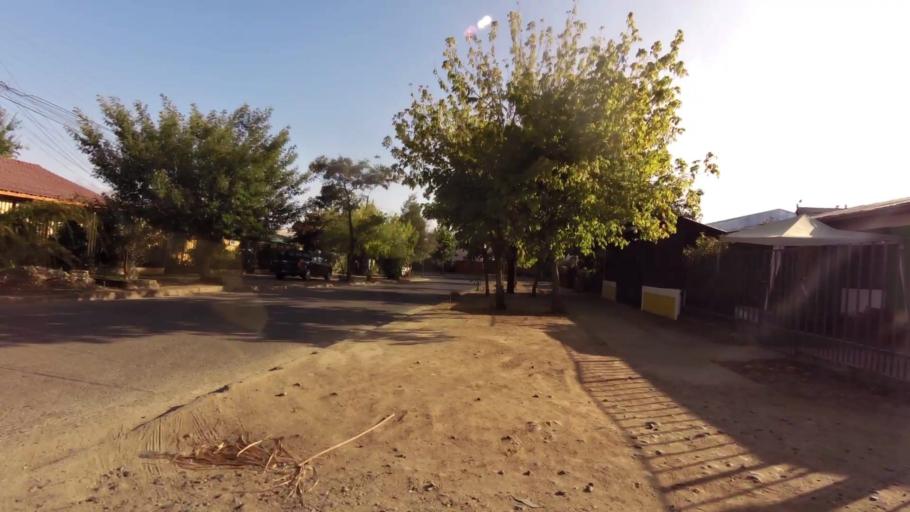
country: CL
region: Maule
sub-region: Provincia de Talca
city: Talca
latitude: -35.4096
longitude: -71.6540
